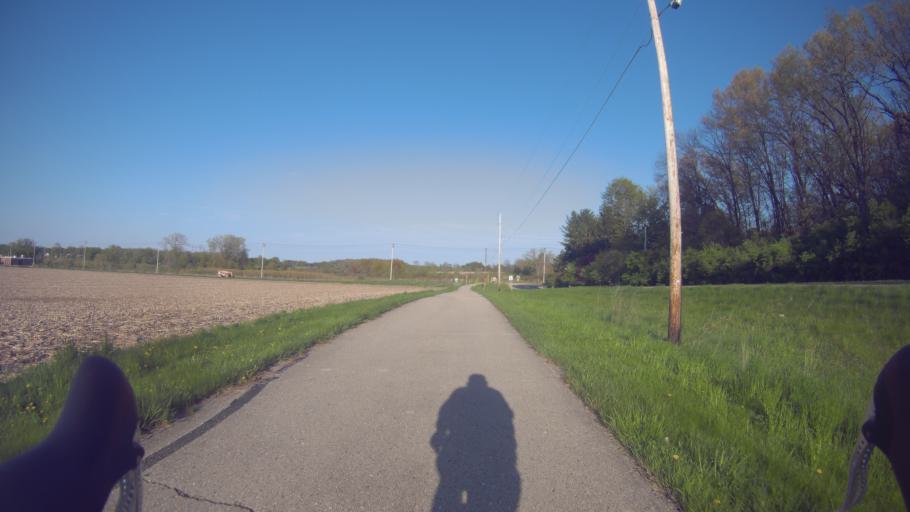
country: US
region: Wisconsin
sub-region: Dane County
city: Monona
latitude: 43.0226
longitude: -89.3671
